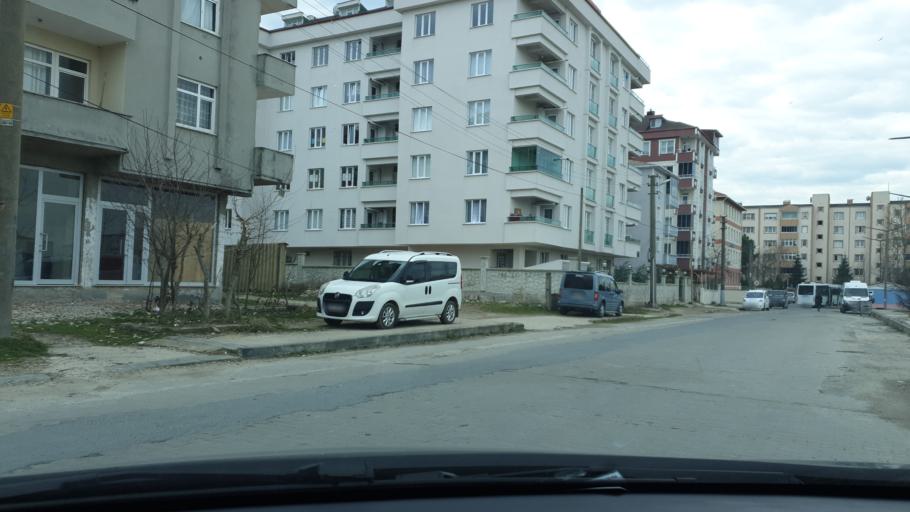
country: TR
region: Tekirdag
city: Cerkezkoey
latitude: 41.2832
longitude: 27.9832
